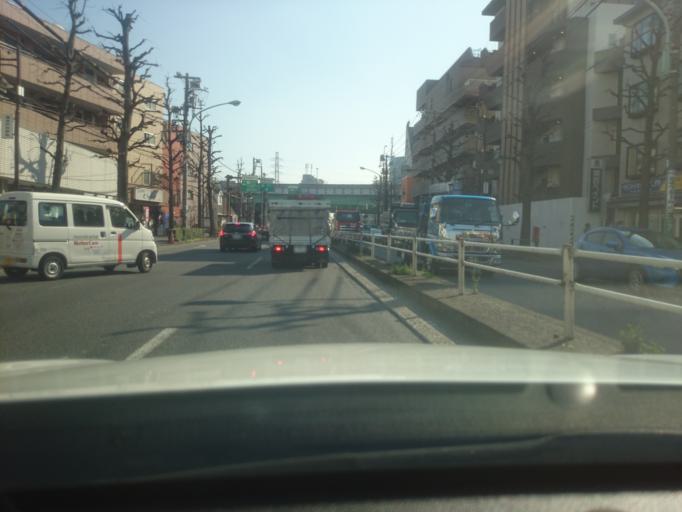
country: JP
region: Tokyo
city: Mitaka-shi
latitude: 35.6784
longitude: 139.6145
